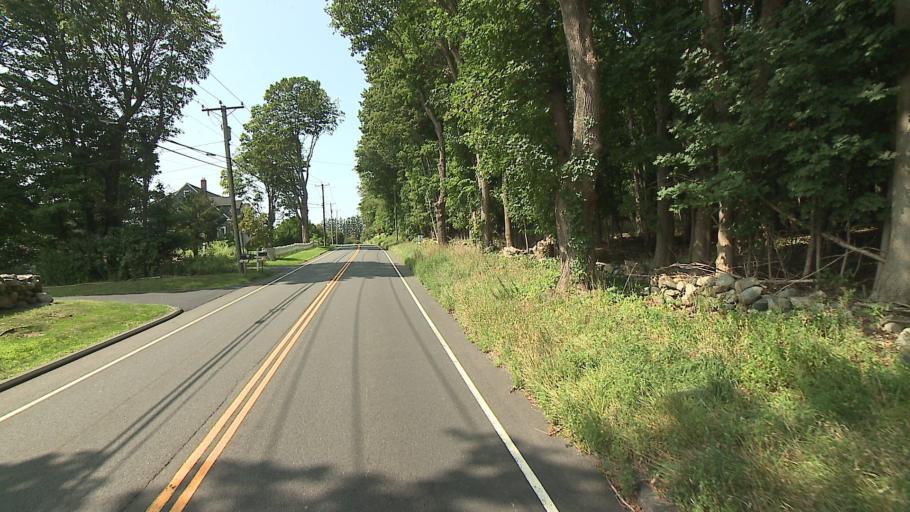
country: US
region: Connecticut
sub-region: Fairfield County
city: Newtown
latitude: 41.4422
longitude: -73.3722
